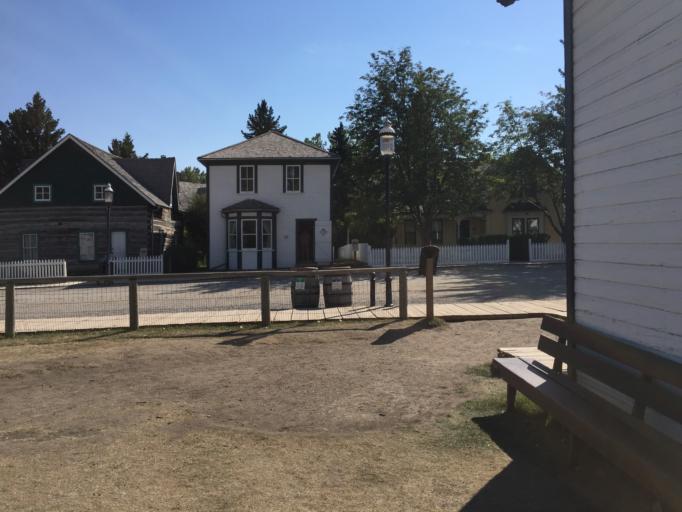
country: CA
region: Alberta
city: Calgary
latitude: 50.9852
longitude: -114.1074
